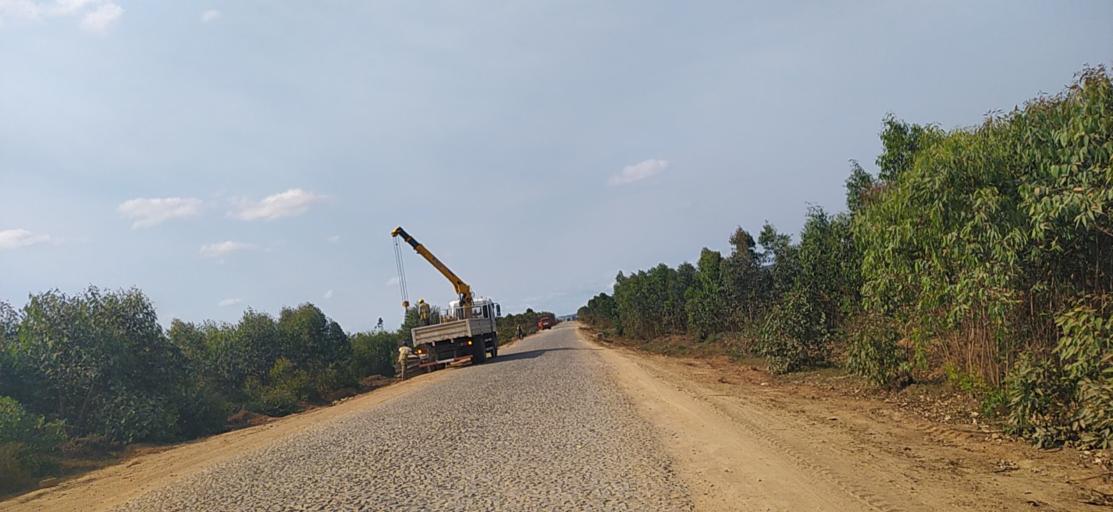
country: MG
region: Alaotra Mangoro
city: Moramanga
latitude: -18.6849
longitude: 48.2715
